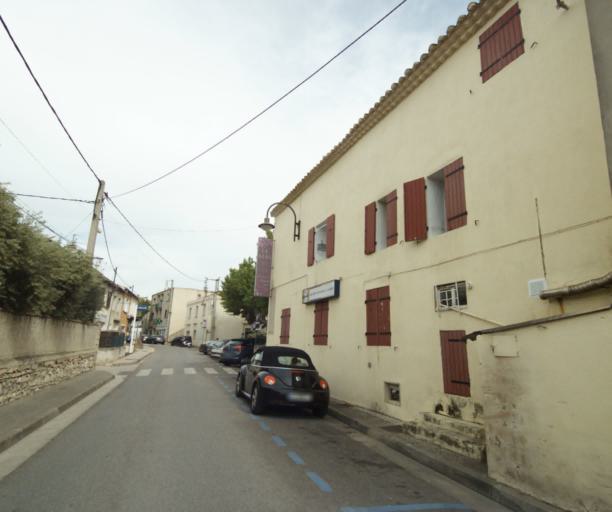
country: FR
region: Provence-Alpes-Cote d'Azur
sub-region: Departement des Bouches-du-Rhone
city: Rognac
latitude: 43.4876
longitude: 5.2254
